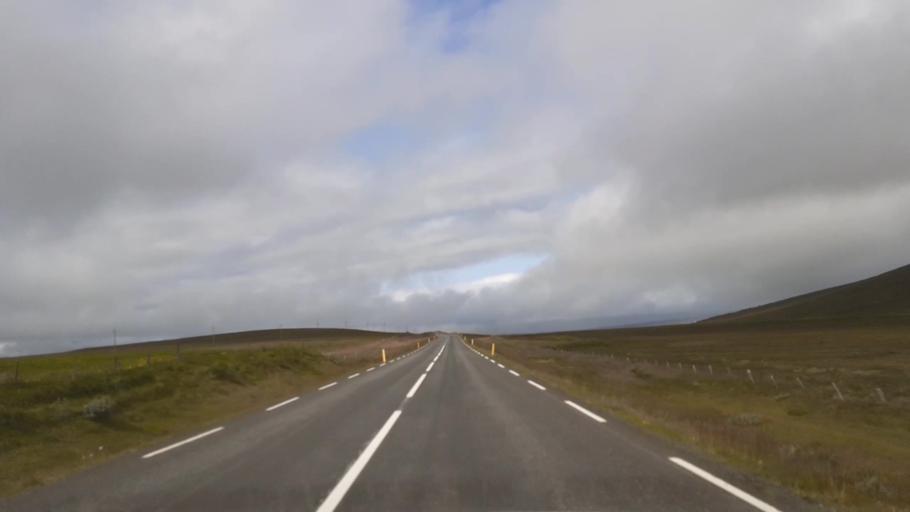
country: IS
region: Northeast
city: Laugar
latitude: 65.8598
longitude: -17.3065
